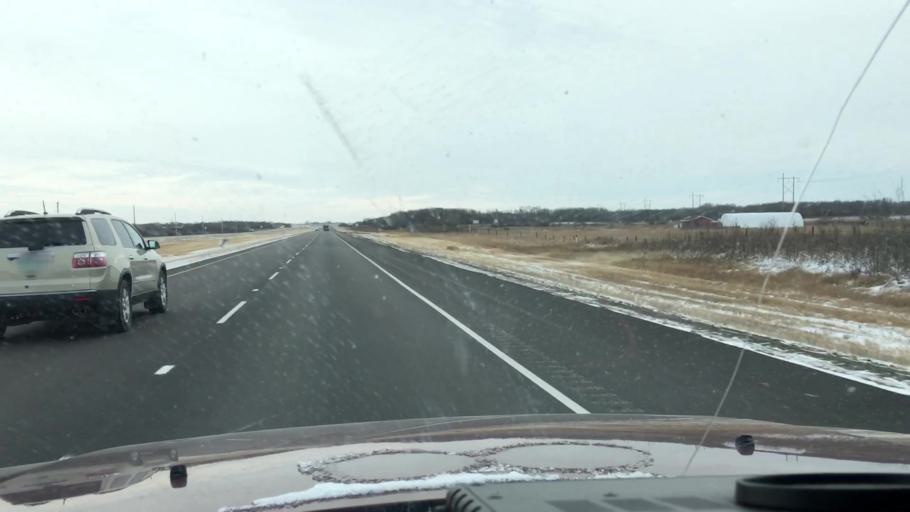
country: CA
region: Saskatchewan
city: Saskatoon
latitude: 51.8844
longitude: -106.5141
